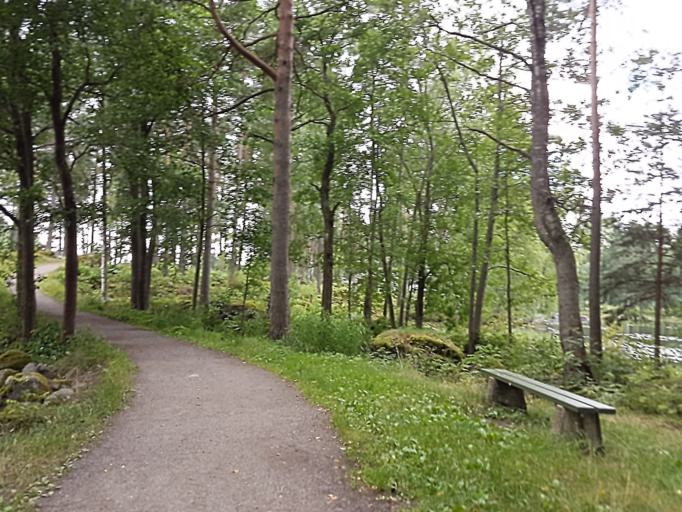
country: FI
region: Pirkanmaa
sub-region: Etelae-Pirkanmaa
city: Valkeakoski
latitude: 61.2720
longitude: 24.0440
